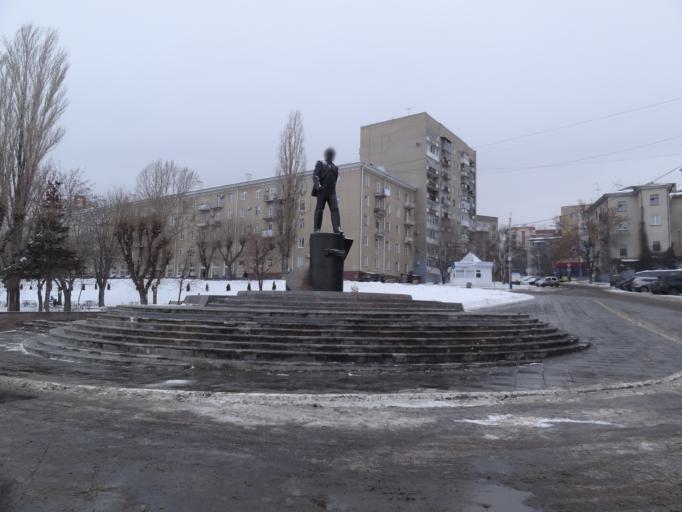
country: RU
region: Saratov
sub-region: Saratovskiy Rayon
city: Saratov
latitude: 51.5257
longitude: 46.0522
